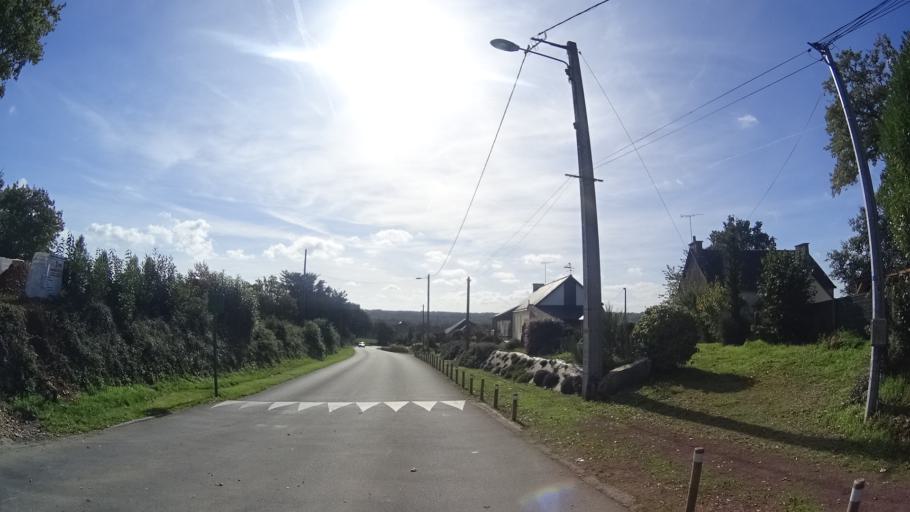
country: FR
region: Brittany
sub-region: Departement du Morbihan
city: Peillac
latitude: 47.7384
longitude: -2.2123
